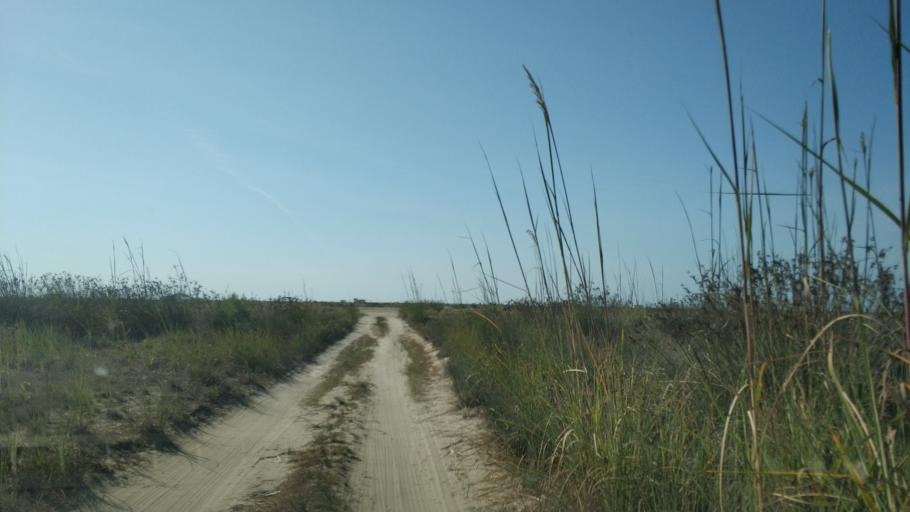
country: AL
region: Fier
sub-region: Rrethi i Lushnjes
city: Divjake
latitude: 40.9619
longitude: 19.4753
